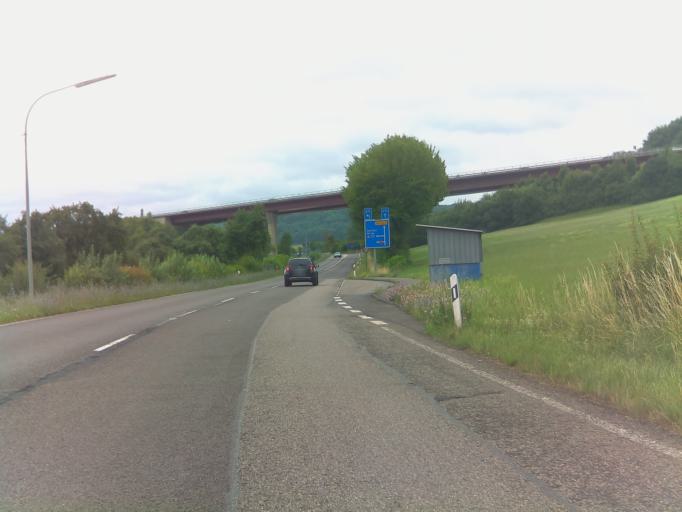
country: DE
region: Saarland
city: Orscholz
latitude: 49.4541
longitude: 6.5146
